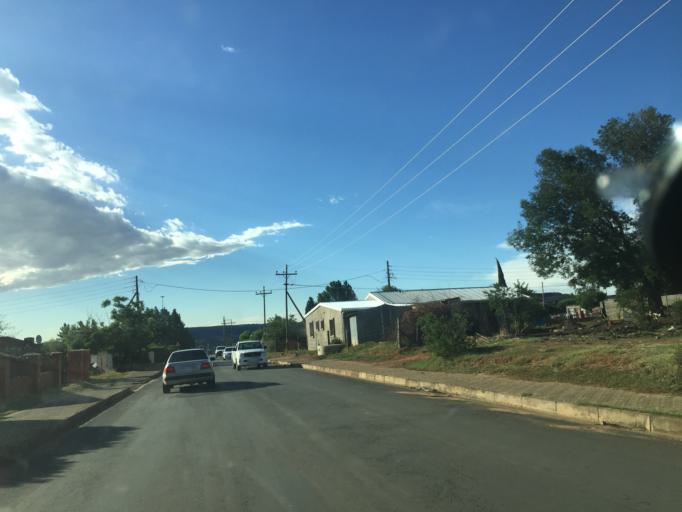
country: LS
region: Maseru
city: Maseru
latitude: -29.2930
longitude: 27.5305
